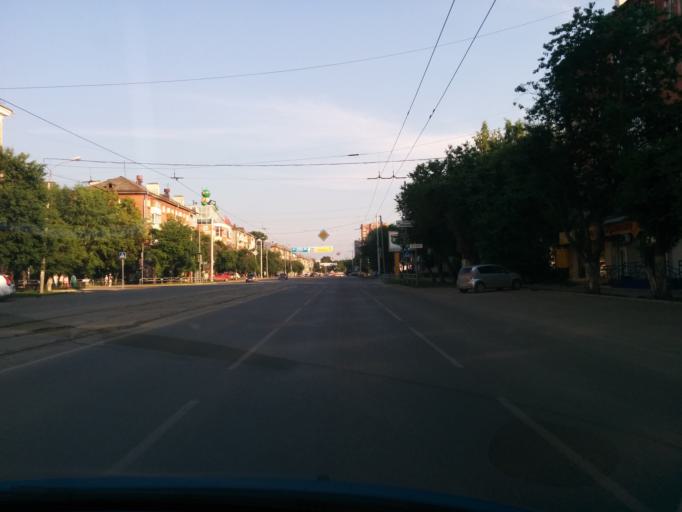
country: RU
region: Perm
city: Perm
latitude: 58.0183
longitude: 56.2780
